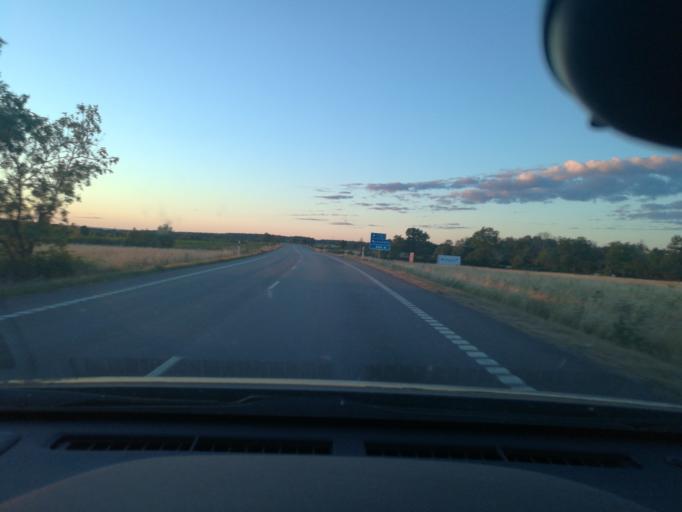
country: SE
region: Kalmar
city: Faerjestaden
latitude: 56.7264
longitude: 16.5385
